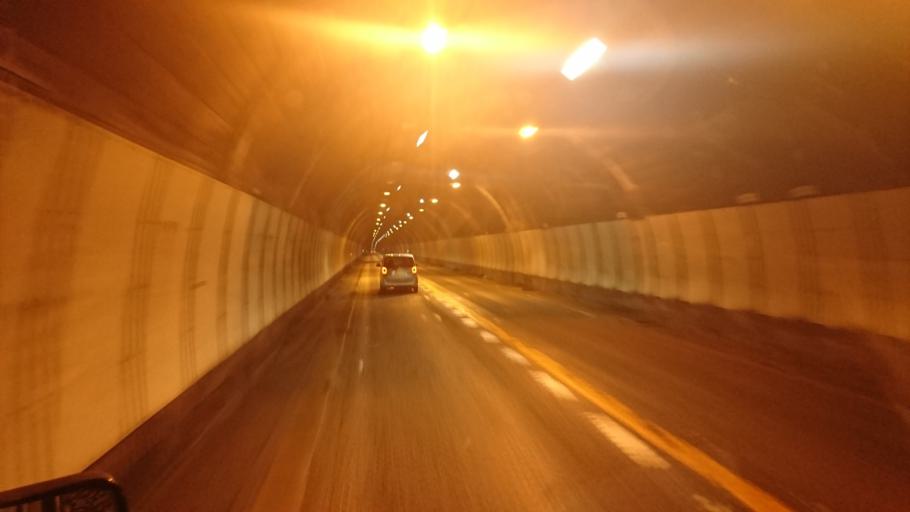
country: JP
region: Hyogo
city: Toyooka
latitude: 35.4852
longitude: 134.5771
